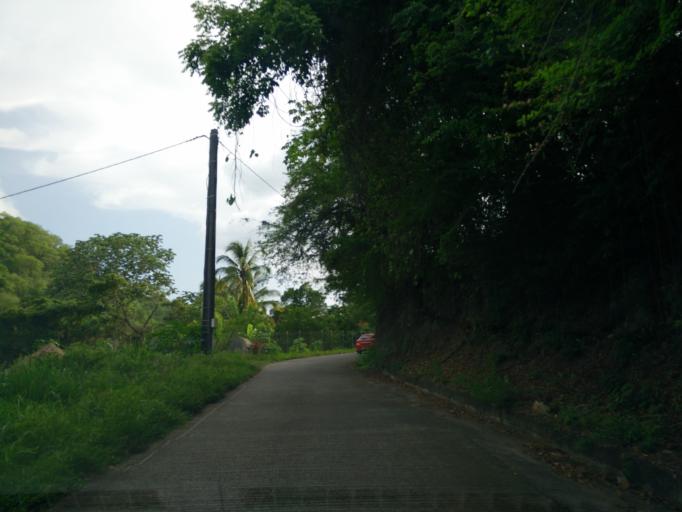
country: MQ
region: Martinique
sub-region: Martinique
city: Saint-Pierre
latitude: 14.7148
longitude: -61.1702
